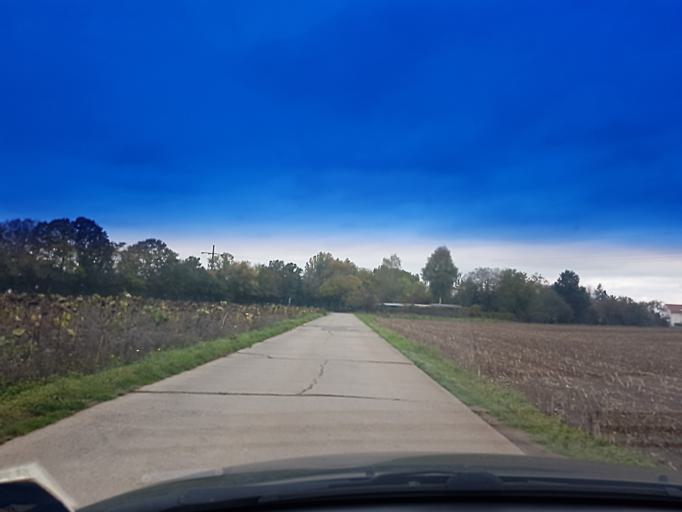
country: DE
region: Bavaria
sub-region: Upper Franconia
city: Bamberg
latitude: 49.8753
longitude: 10.9147
